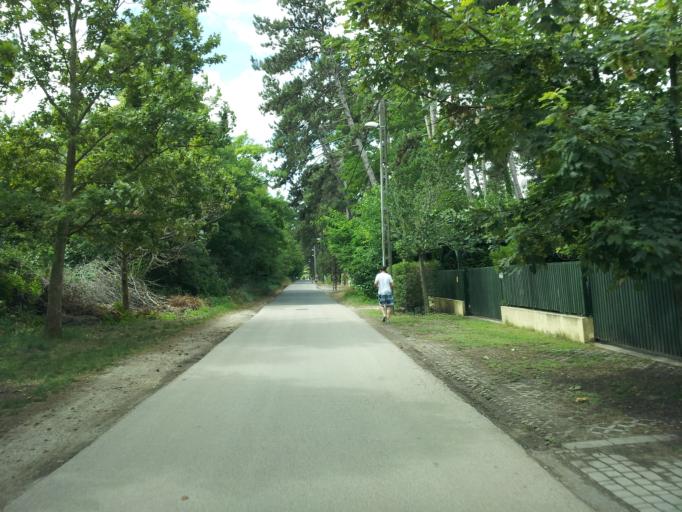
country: HU
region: Somogy
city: Balatonszabadi
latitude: 46.9429
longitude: 18.1342
